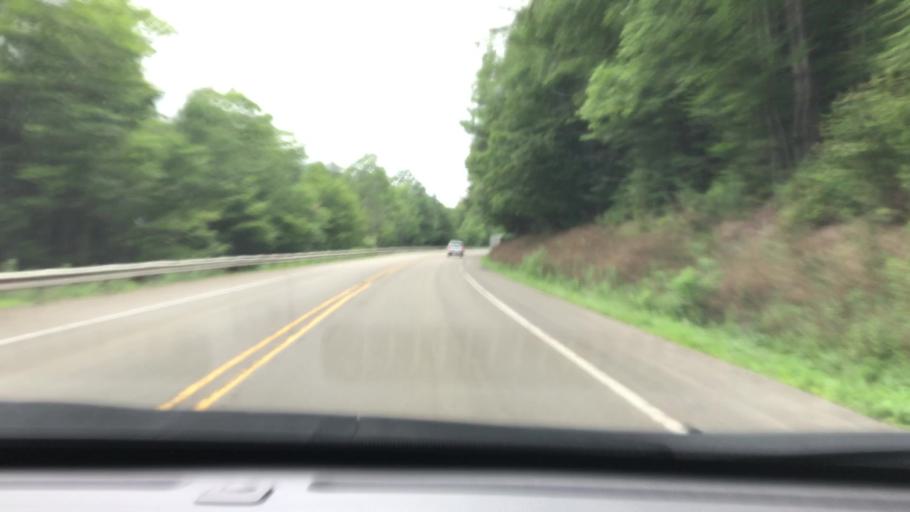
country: US
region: Pennsylvania
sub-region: McKean County
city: Kane
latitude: 41.6610
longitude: -78.6816
